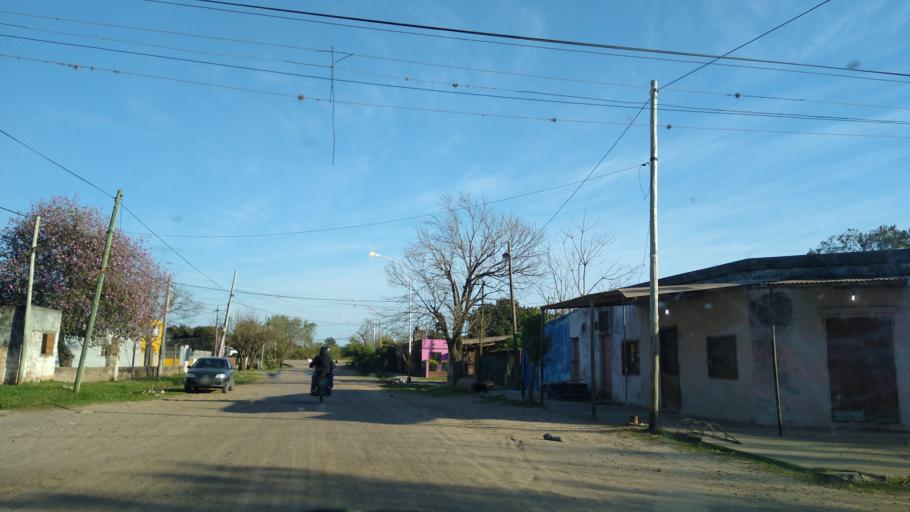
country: AR
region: Chaco
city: Barranqueras
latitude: -27.4704
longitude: -58.9343
